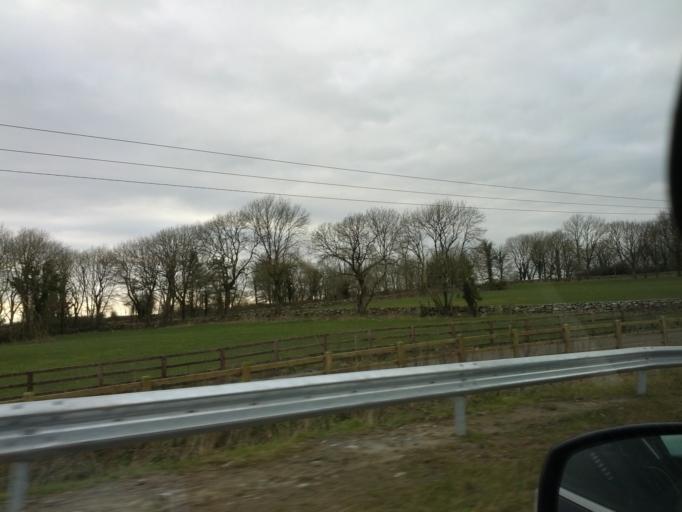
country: IE
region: Connaught
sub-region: County Galway
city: Gort
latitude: 53.1656
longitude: -8.8526
